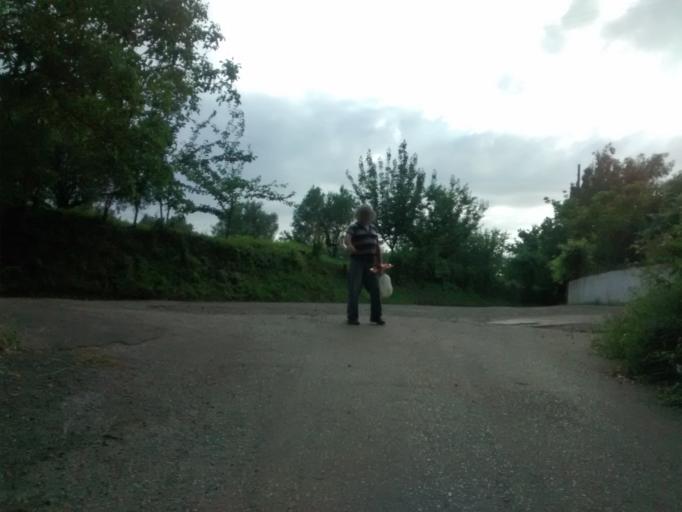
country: IT
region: Calabria
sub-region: Provincia di Catanzaro
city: Jacurso
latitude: 38.8852
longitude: 16.4010
